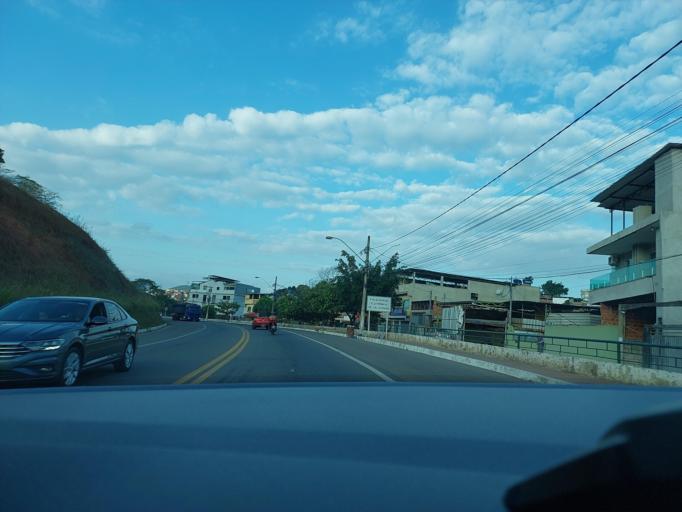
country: BR
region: Minas Gerais
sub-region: Muriae
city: Muriae
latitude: -21.1295
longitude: -42.3600
